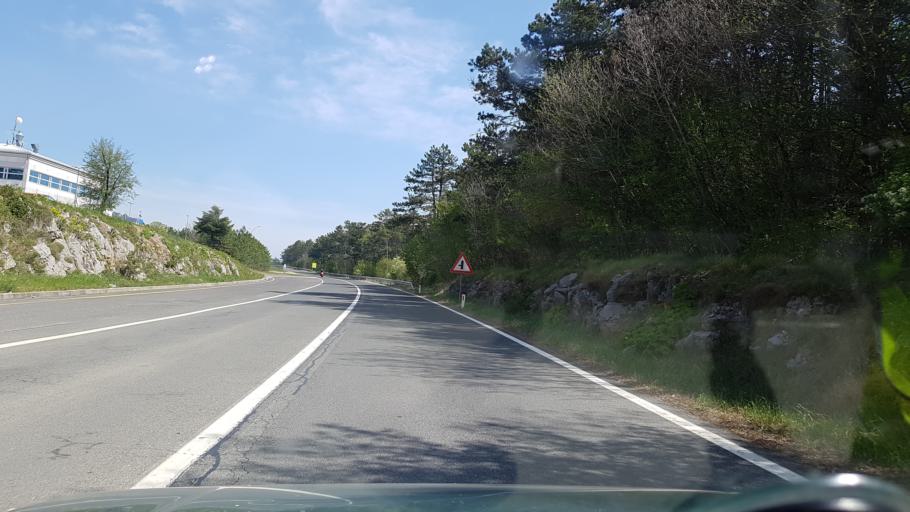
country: SI
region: Hrpelje-Kozina
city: Kozina
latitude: 45.6124
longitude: 13.9425
